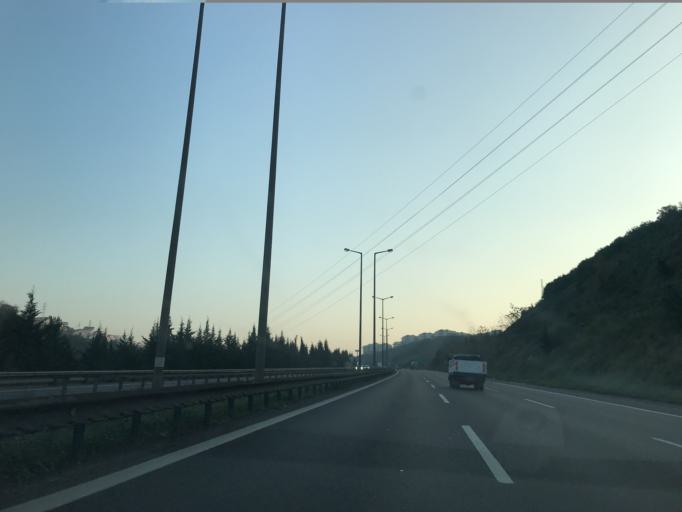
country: TR
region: Kocaeli
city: Izmit
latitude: 40.7771
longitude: 29.9174
